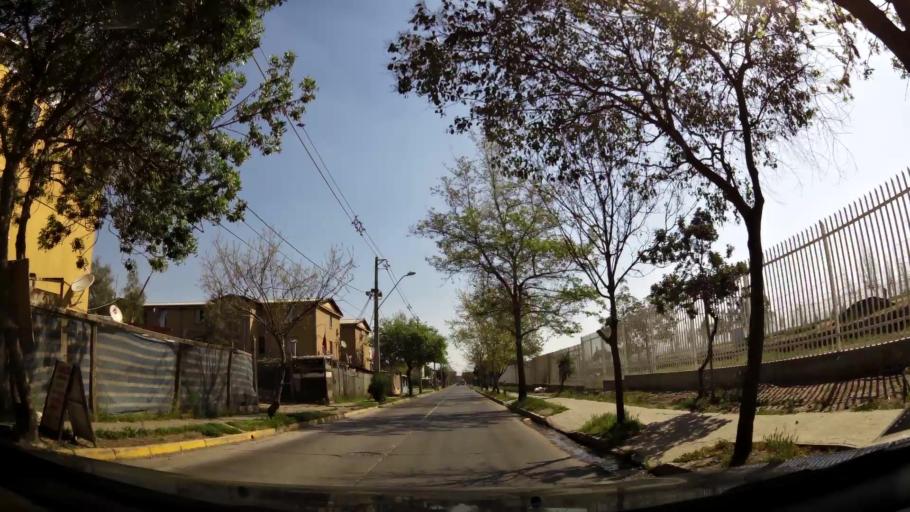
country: CL
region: Santiago Metropolitan
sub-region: Provincia de Cordillera
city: Puente Alto
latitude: -33.6257
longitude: -70.6155
